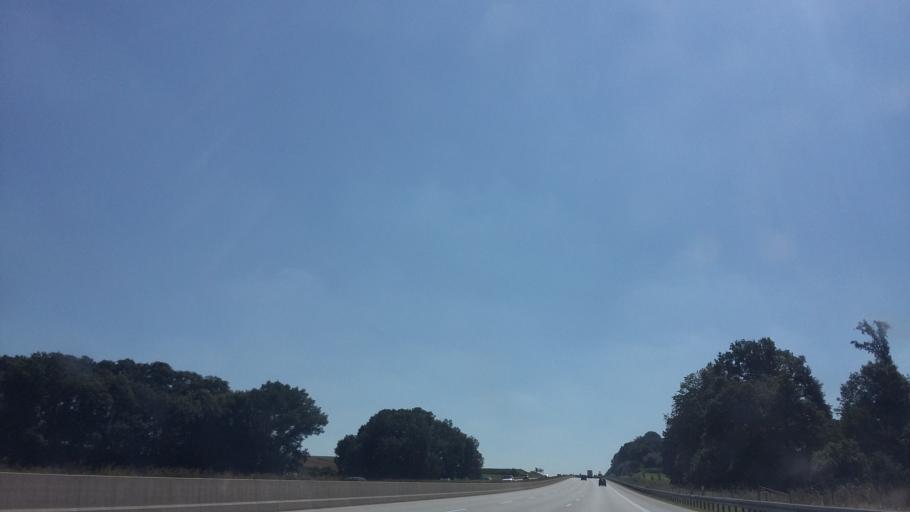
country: DE
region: Bavaria
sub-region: Swabia
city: Dasing
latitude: 48.3814
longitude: 11.0848
